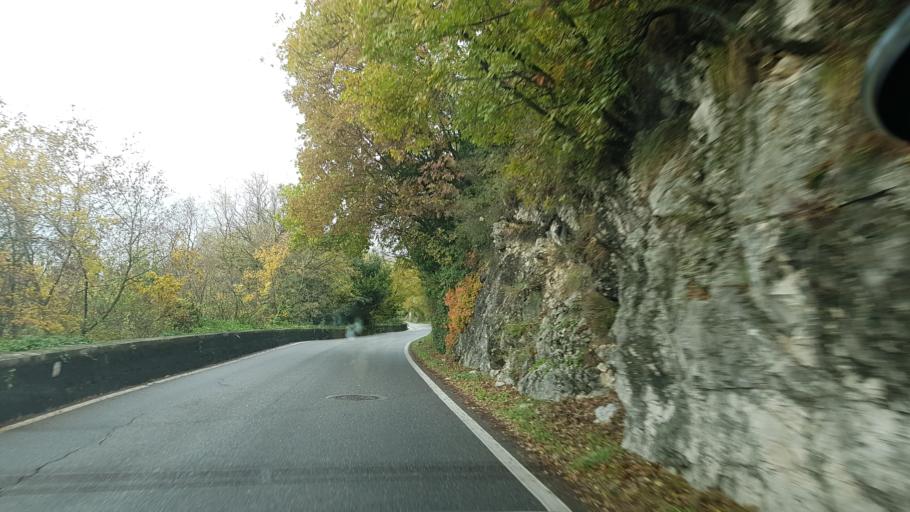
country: IT
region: Friuli Venezia Giulia
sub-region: Provincia di Trieste
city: Prosecco-Contovello
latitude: 45.6986
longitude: 13.7378
